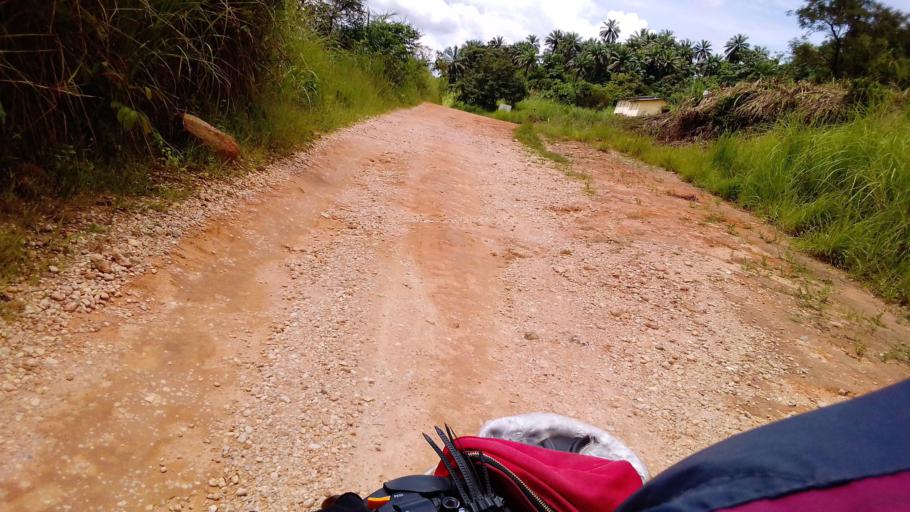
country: SL
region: Eastern Province
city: Koyima
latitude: 8.6904
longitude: -11.0085
